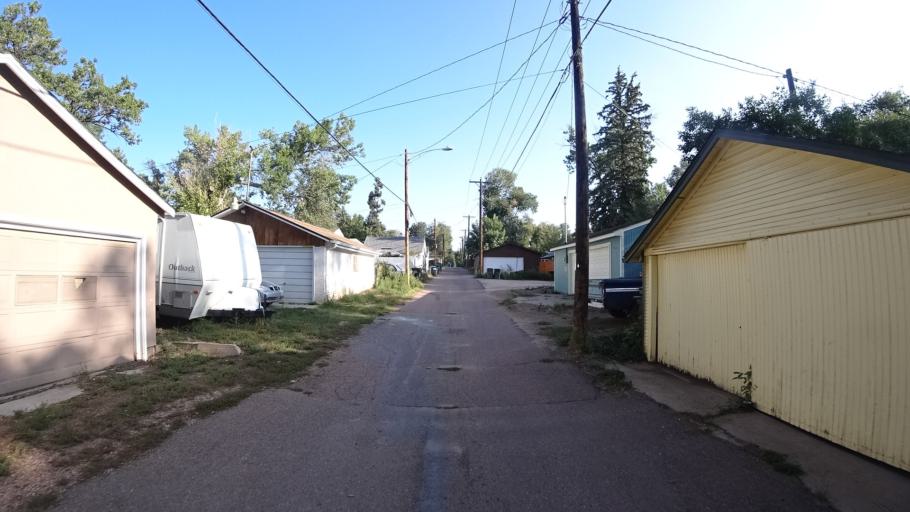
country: US
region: Colorado
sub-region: El Paso County
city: Colorado Springs
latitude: 38.8395
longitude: -104.8343
